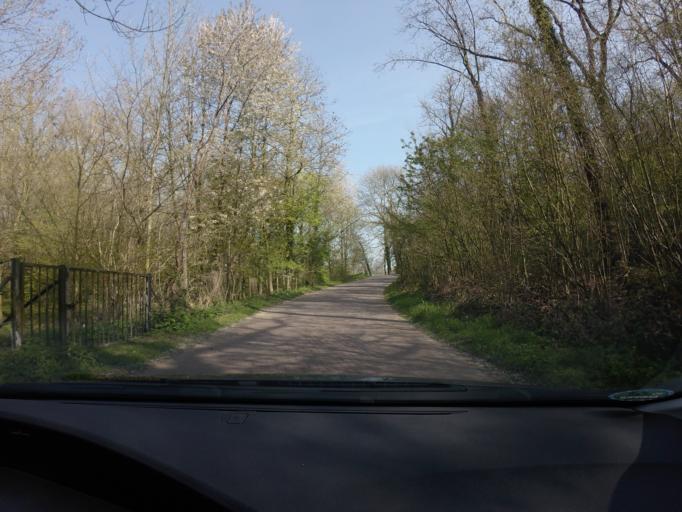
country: NL
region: Limburg
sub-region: Gemeente Meerssen
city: Meerssen
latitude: 50.8941
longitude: 5.7674
